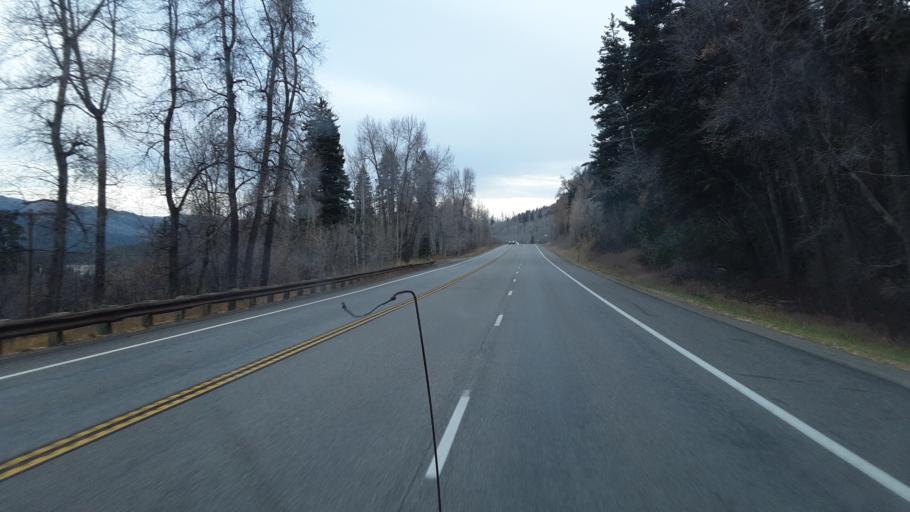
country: US
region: Colorado
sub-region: La Plata County
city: Durango
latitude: 37.5507
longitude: -107.8243
